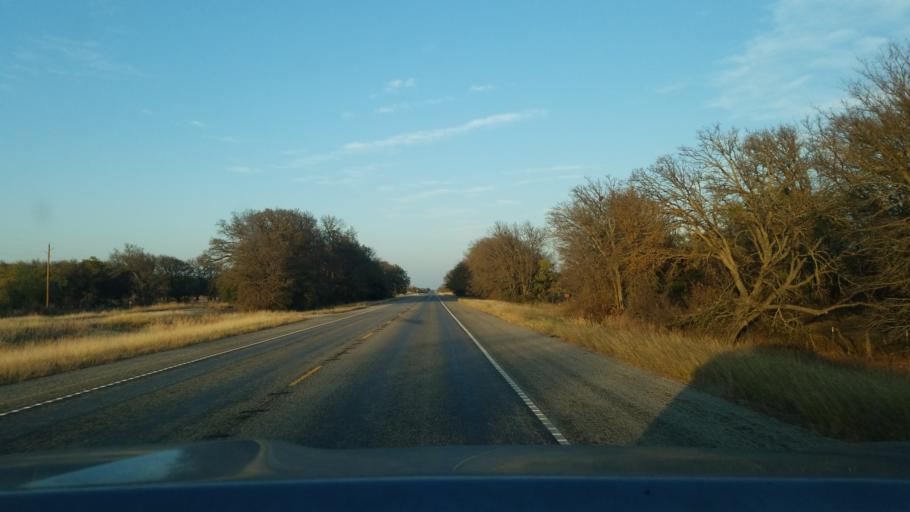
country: US
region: Texas
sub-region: Eastland County
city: Cisco
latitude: 32.4134
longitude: -98.9439
